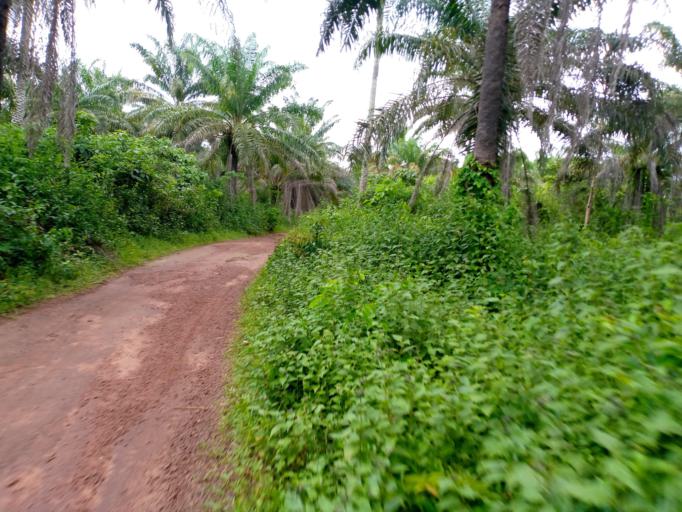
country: SL
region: Northern Province
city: Mange
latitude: 8.9838
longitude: -12.7134
